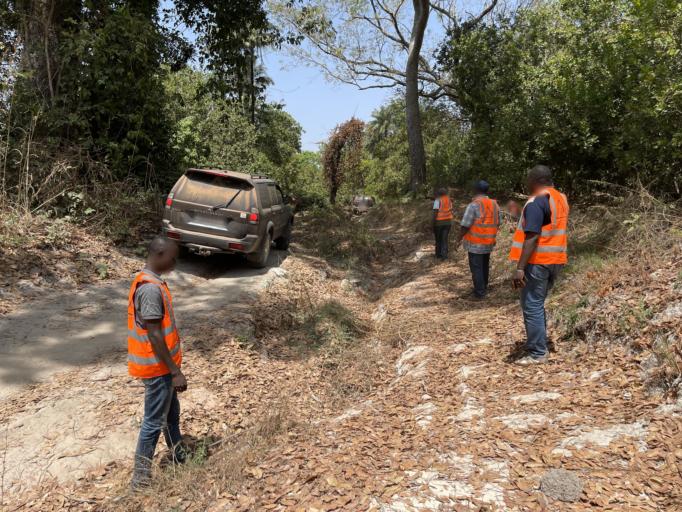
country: GW
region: Oio
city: Bissora
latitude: 12.4332
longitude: -15.6154
